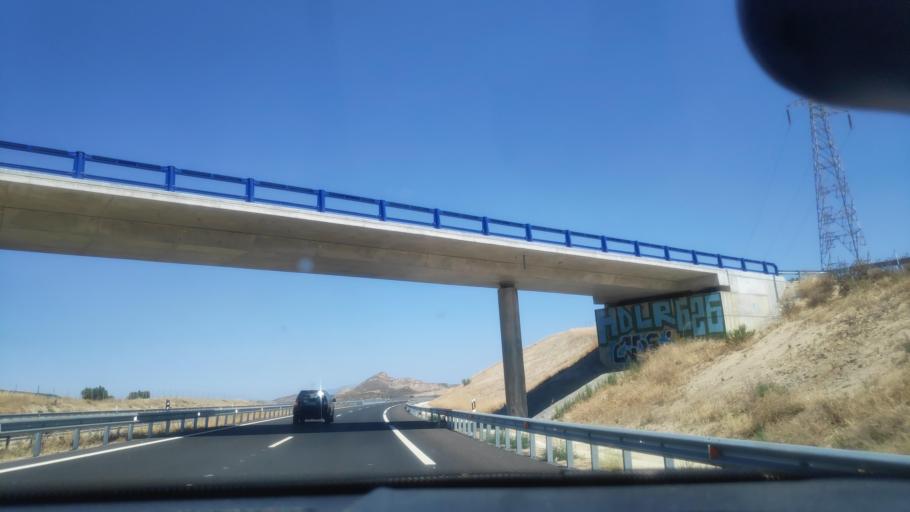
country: ES
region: Andalusia
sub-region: Provincia de Granada
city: Otura
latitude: 37.0735
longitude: -3.6603
